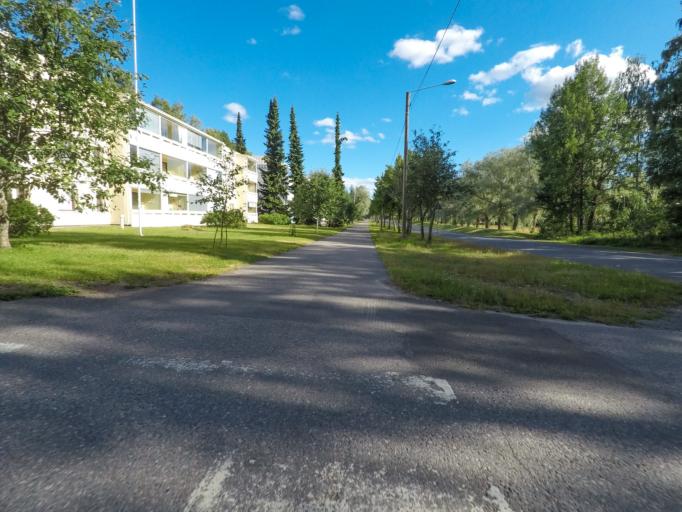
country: FI
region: South Karelia
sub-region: Lappeenranta
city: Lappeenranta
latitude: 61.0805
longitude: 28.1492
